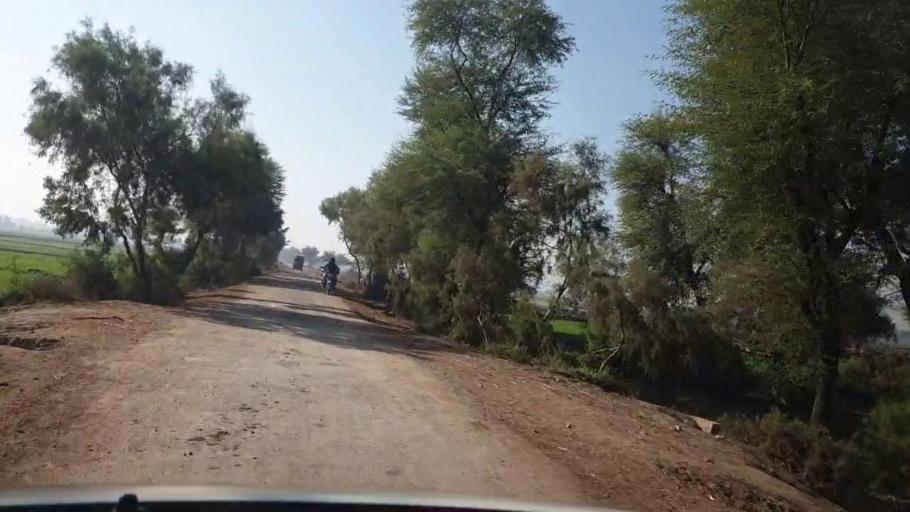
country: PK
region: Sindh
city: Dadu
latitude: 26.6471
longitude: 67.8220
